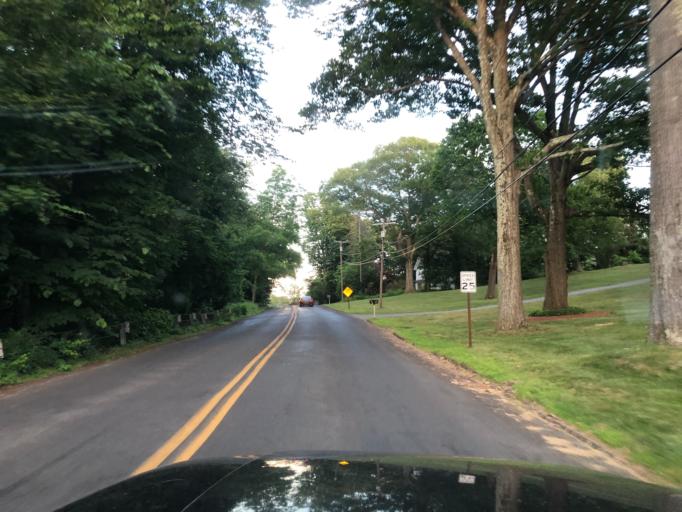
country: US
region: Connecticut
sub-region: Middlesex County
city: Durham
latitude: 41.5323
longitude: -72.7015
